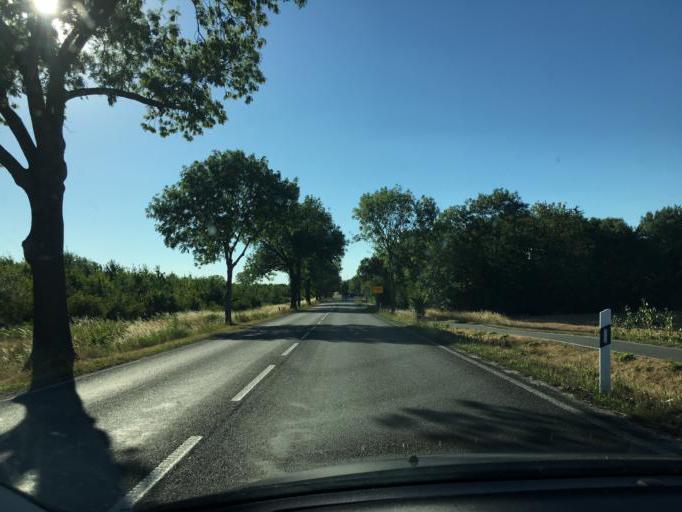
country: DE
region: Saxony
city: Grossposna
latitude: 51.2703
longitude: 12.4839
